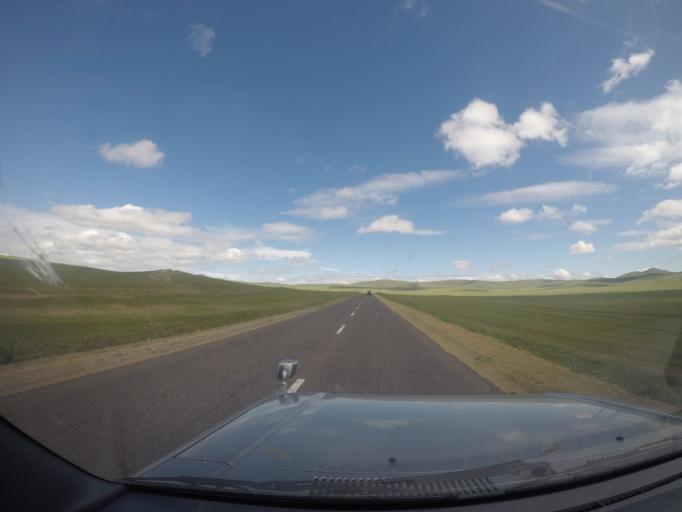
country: MN
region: Hentiy
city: Modot
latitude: 47.6006
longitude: 109.2328
